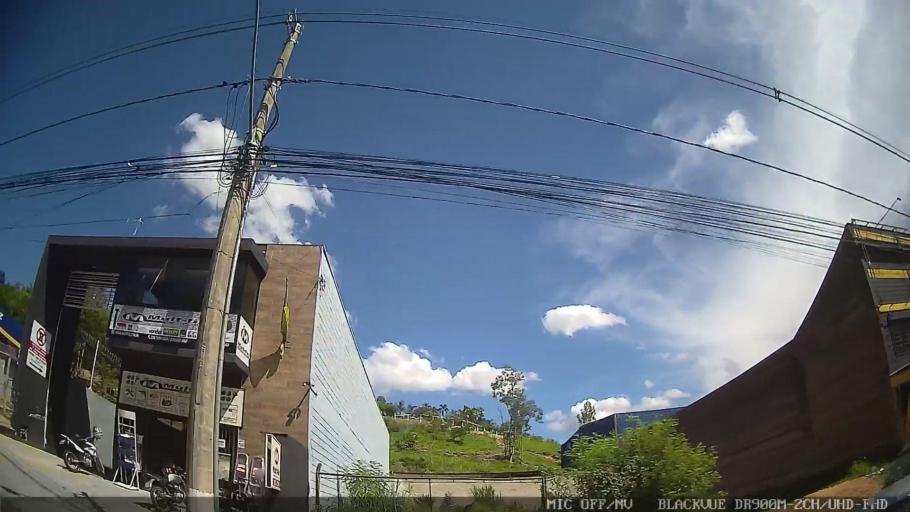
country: BR
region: Sao Paulo
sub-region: Pedreira
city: Pedreira
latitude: -22.7368
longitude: -46.8887
